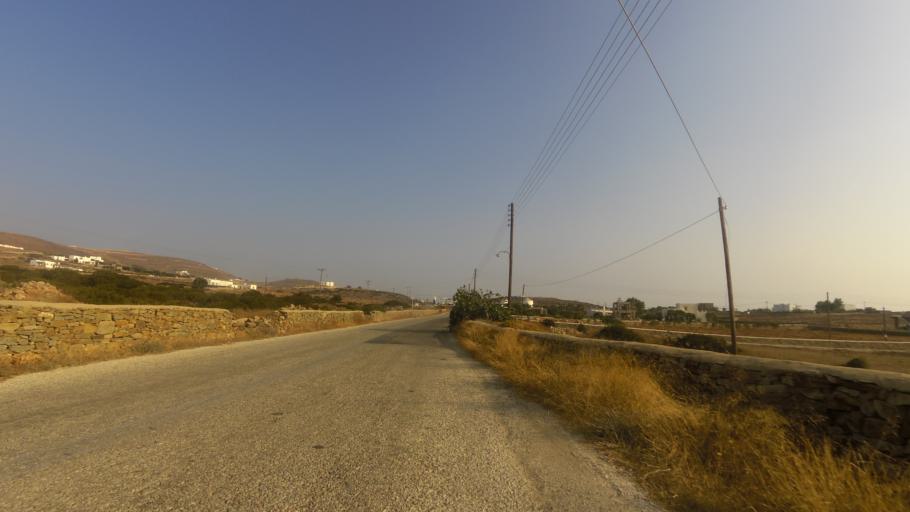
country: GR
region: South Aegean
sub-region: Nomos Kykladon
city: Antiparos
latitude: 37.0255
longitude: 25.0768
